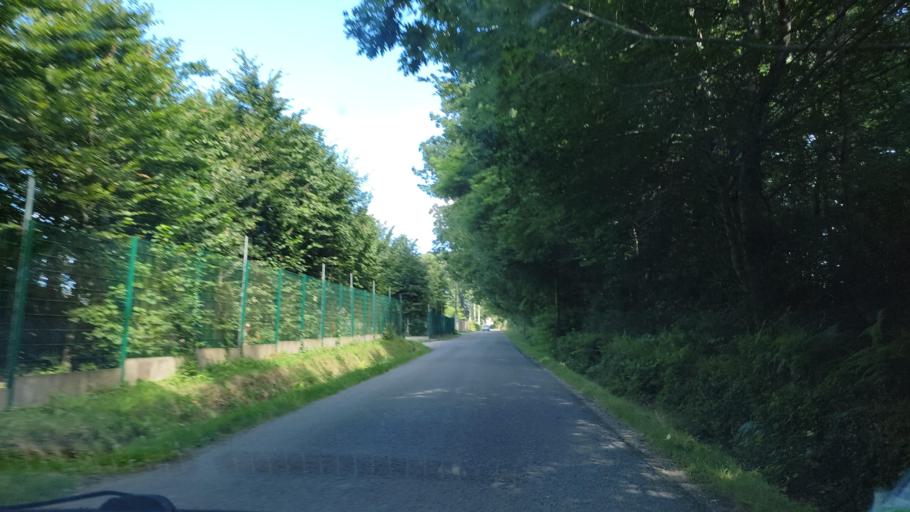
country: FR
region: Limousin
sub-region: Departement de la Haute-Vienne
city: Couzeix
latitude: 45.8547
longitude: 1.1894
